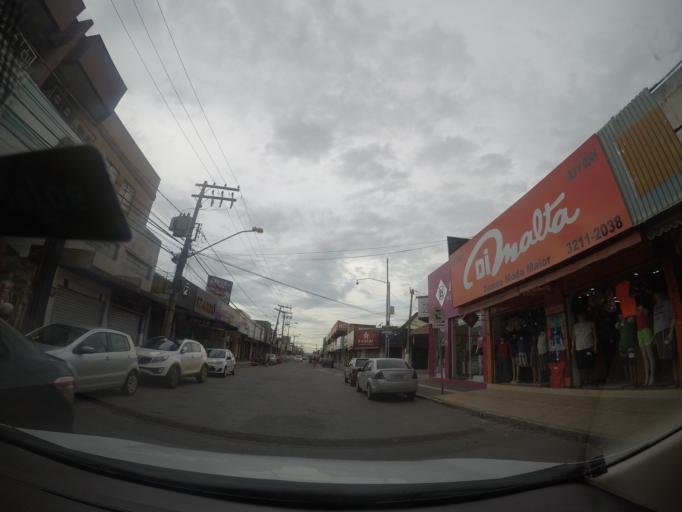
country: BR
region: Goias
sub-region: Goiania
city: Goiania
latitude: -16.6618
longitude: -49.2762
